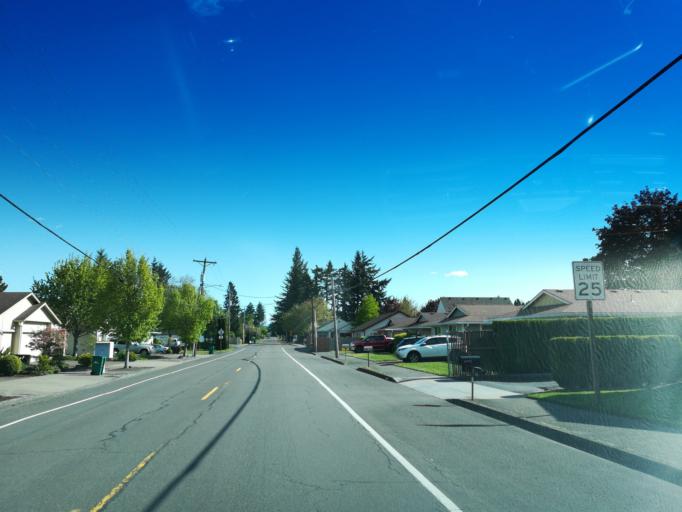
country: US
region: Oregon
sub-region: Multnomah County
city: Troutdale
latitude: 45.5333
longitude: -122.3934
